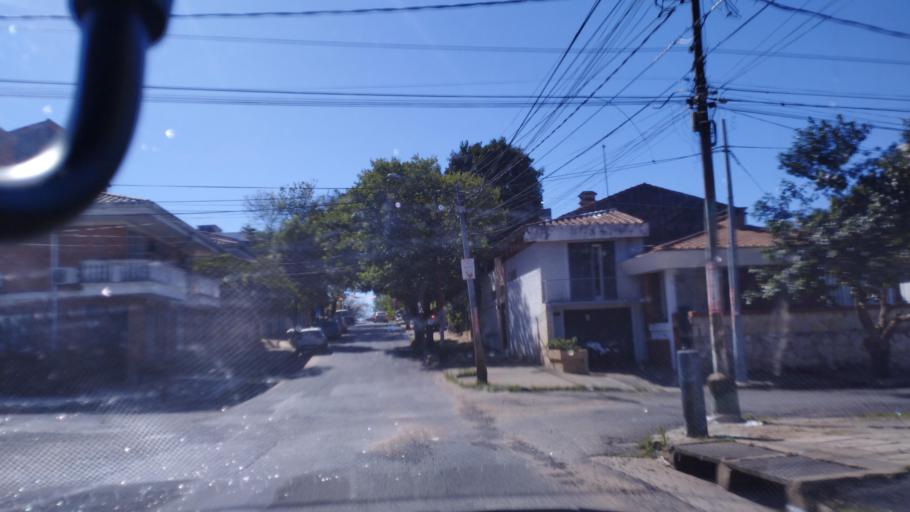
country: PY
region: Asuncion
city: Asuncion
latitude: -25.2966
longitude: -57.6140
